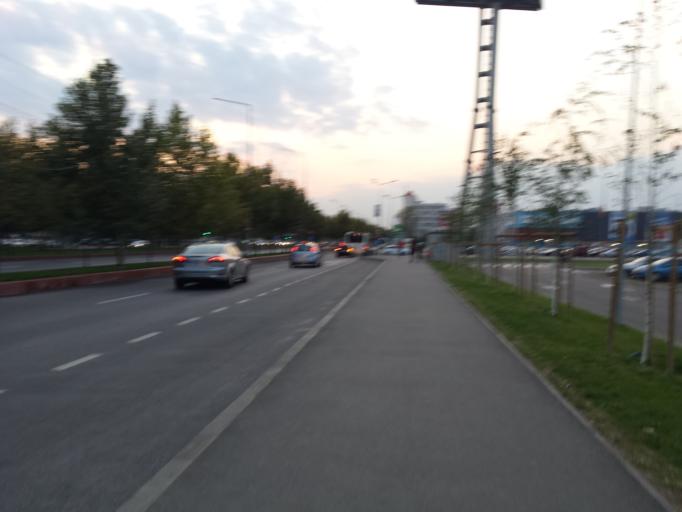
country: RO
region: Ilfov
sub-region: Comuna Glina
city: Catelu
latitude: 44.4060
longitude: 26.2058
